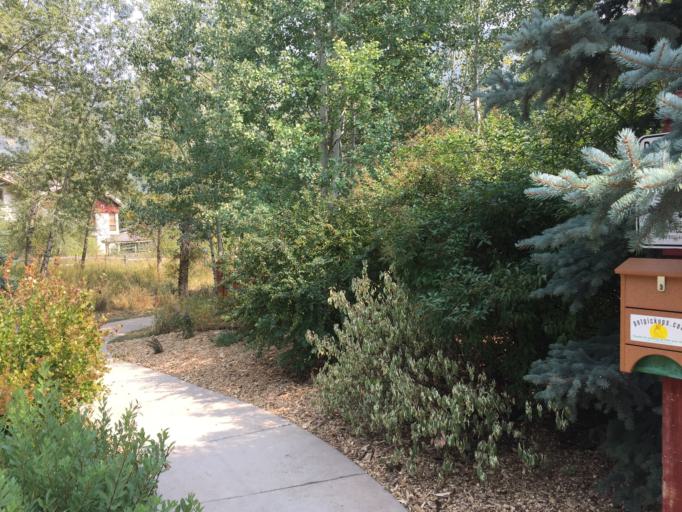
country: US
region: Colorado
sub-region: Eagle County
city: Vail
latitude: 39.6341
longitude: -106.4141
